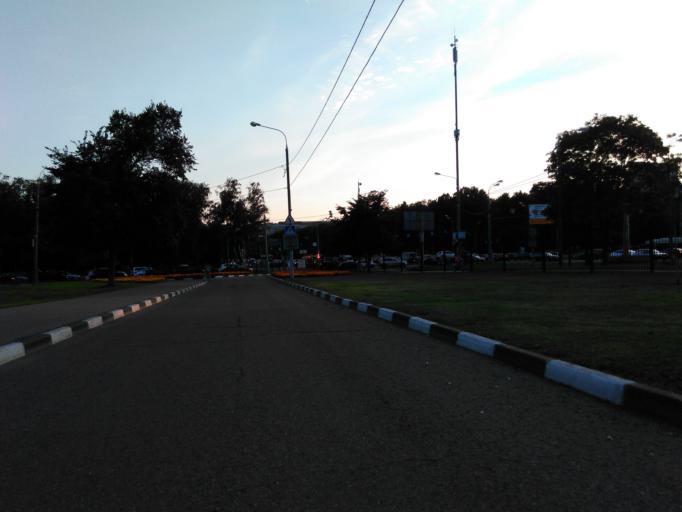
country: RU
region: Moscow
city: Luzhniki
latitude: 55.7012
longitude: 37.5481
